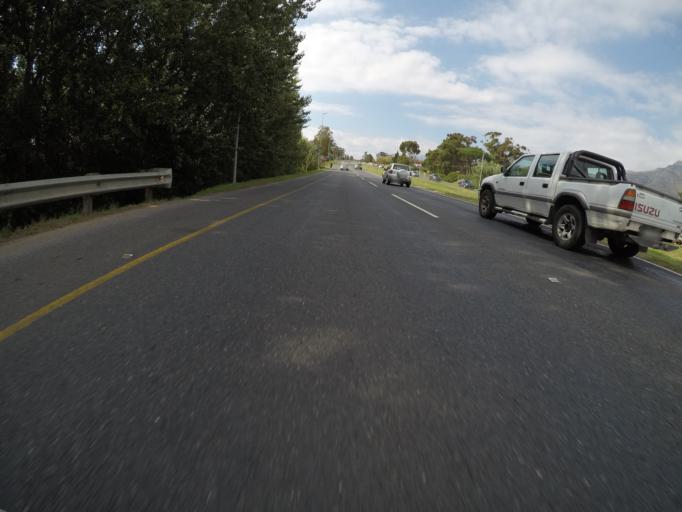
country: ZA
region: Western Cape
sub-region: Cape Winelands District Municipality
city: Stellenbosch
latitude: -33.9721
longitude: 18.8427
